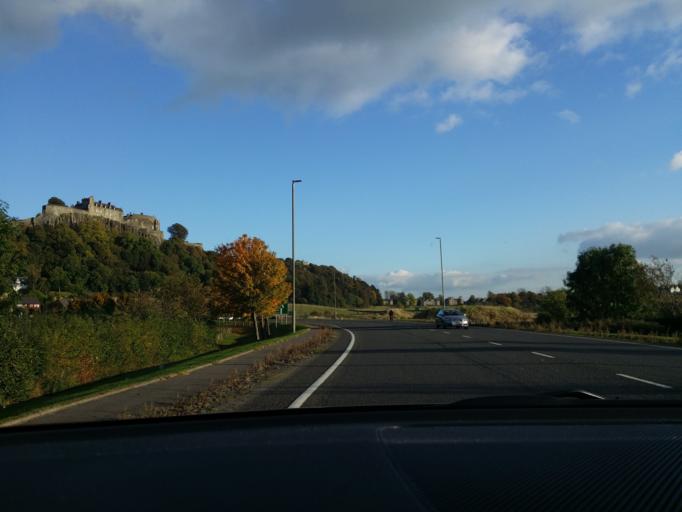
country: GB
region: Scotland
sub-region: Stirling
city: Stirling
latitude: 56.1254
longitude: -3.9577
